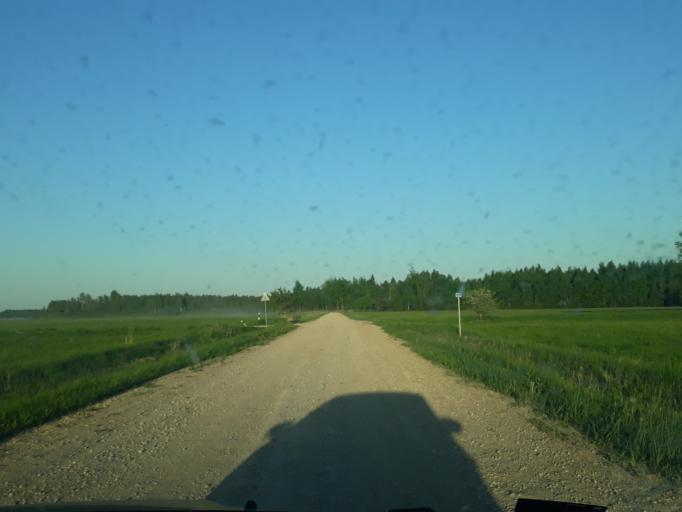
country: EE
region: Paernumaa
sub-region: Tootsi vald
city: Tootsi
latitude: 58.5809
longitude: 24.9095
